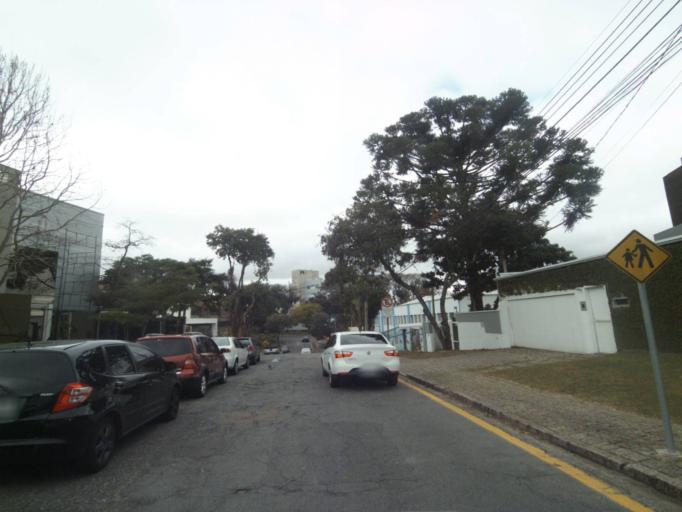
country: BR
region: Parana
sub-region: Curitiba
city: Curitiba
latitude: -25.4541
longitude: -49.2989
